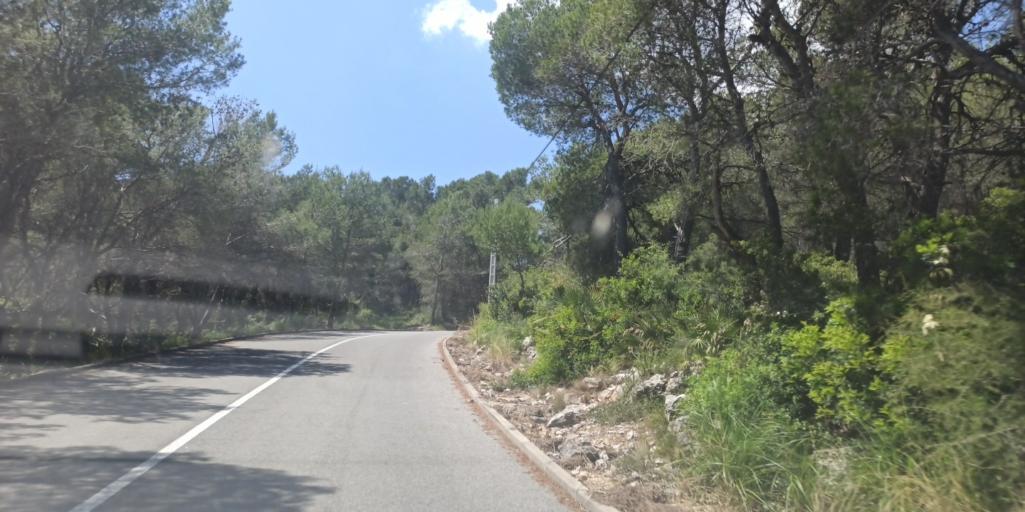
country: ES
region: Catalonia
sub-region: Provincia de Barcelona
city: Vilafranca del Penedes
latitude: 41.2961
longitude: 1.7095
